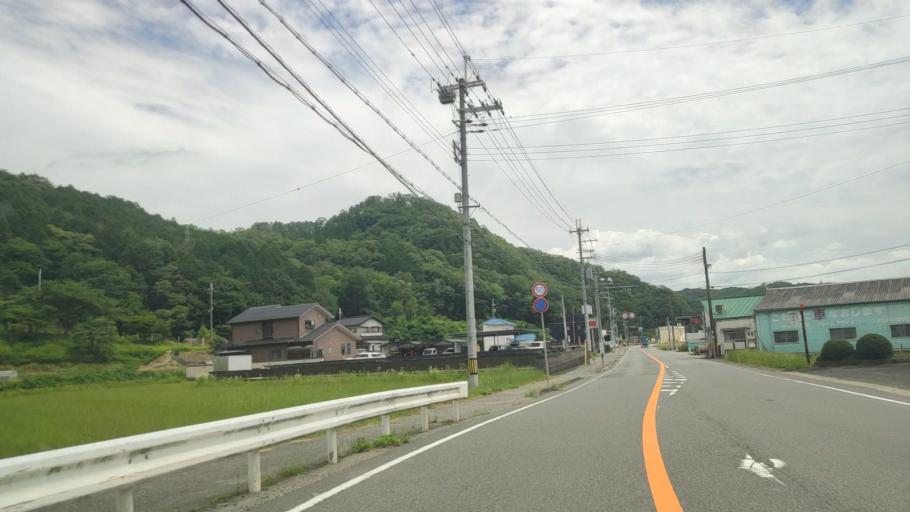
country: JP
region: Hyogo
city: Yamazakicho-nakabirose
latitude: 35.0285
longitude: 134.3698
